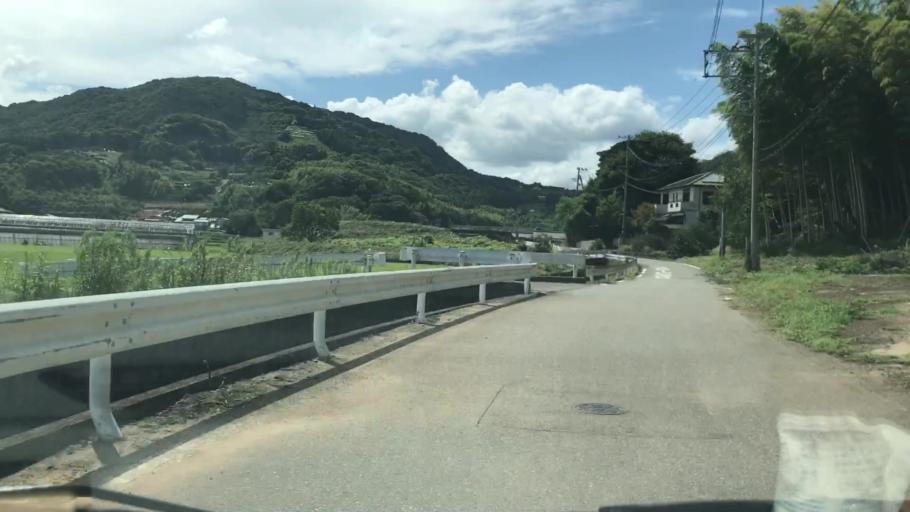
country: JP
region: Saga Prefecture
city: Saga-shi
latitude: 33.2343
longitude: 130.1760
